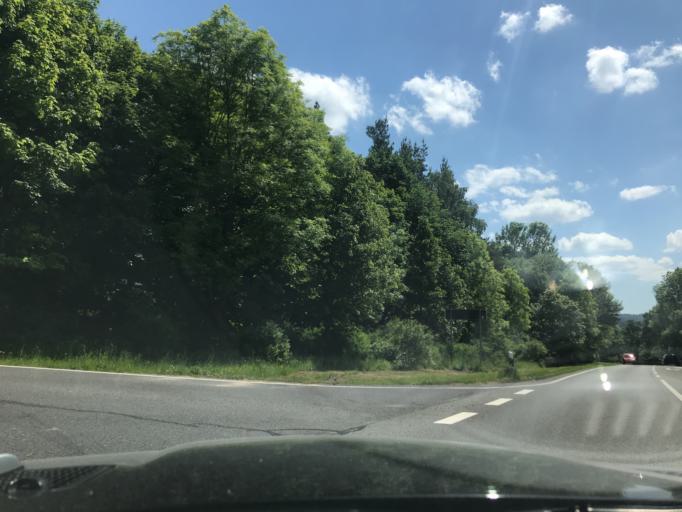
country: DE
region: Thuringia
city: Martinroda
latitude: 50.7039
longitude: 10.8941
